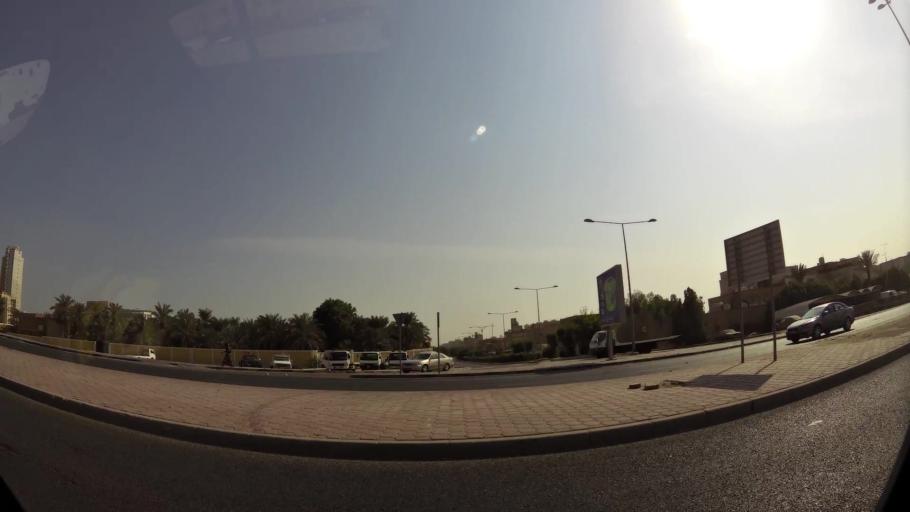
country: KW
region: Al Ahmadi
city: Al Fintas
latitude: 29.1603
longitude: 48.1076
